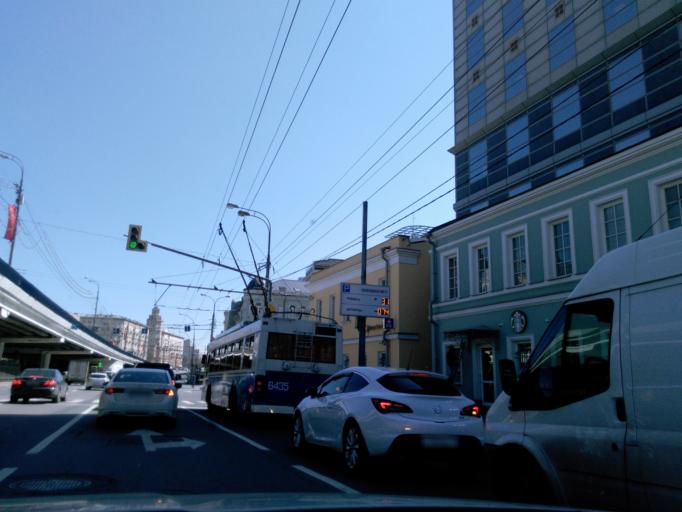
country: RU
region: Moscow
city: Moscow
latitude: 55.7735
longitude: 37.6202
